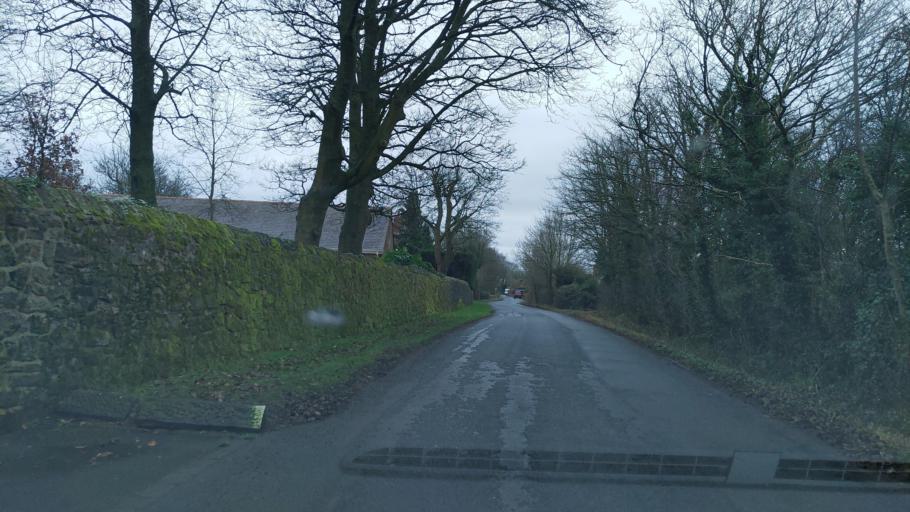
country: GB
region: England
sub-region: Lancashire
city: Clayton-le-Woods
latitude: 53.7032
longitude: -2.6604
